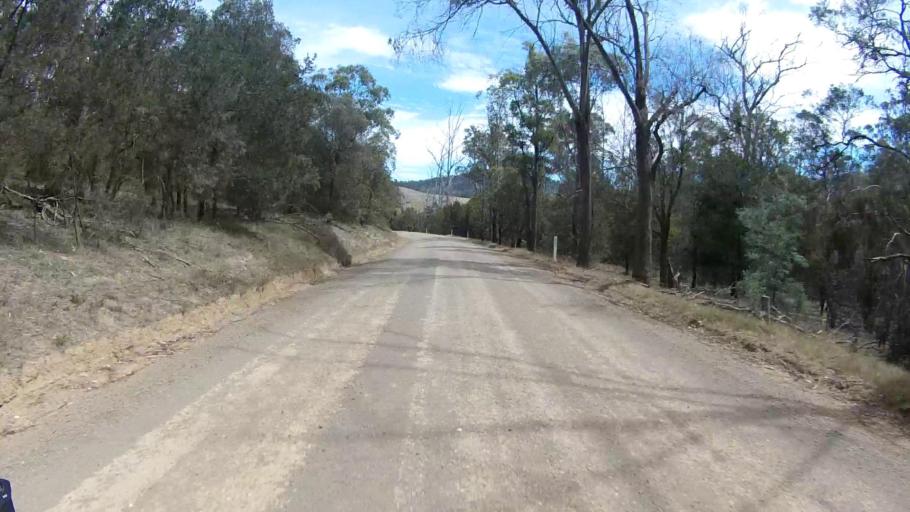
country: AU
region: Tasmania
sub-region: Sorell
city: Sorell
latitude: -42.8017
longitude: 147.6677
